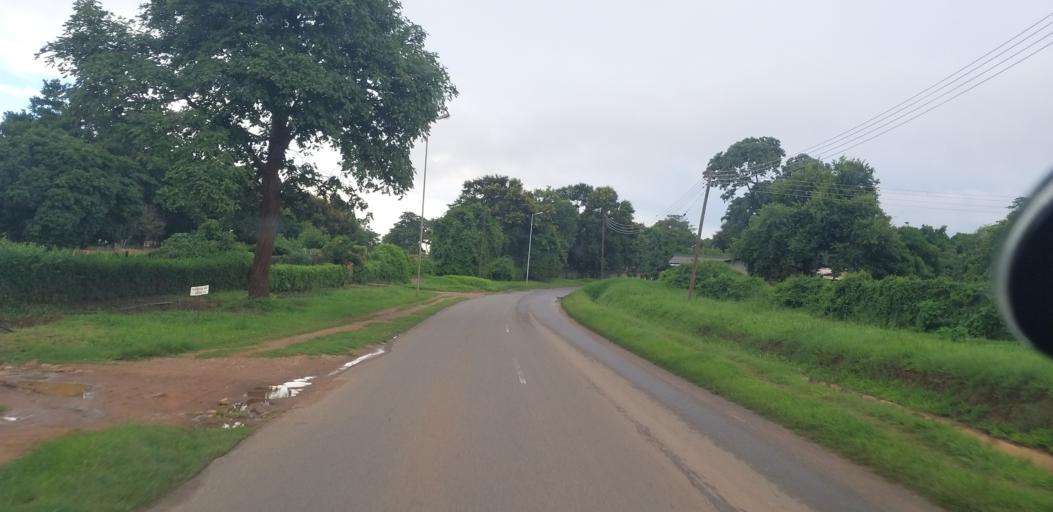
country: ZM
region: Lusaka
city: Lusaka
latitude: -15.4287
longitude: 28.3326
